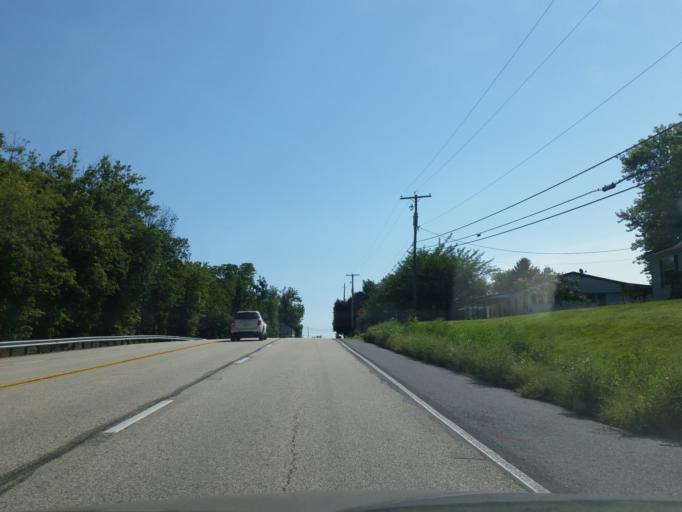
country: US
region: Pennsylvania
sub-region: Lebanon County
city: Jonestown
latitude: 40.4434
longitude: -76.5339
